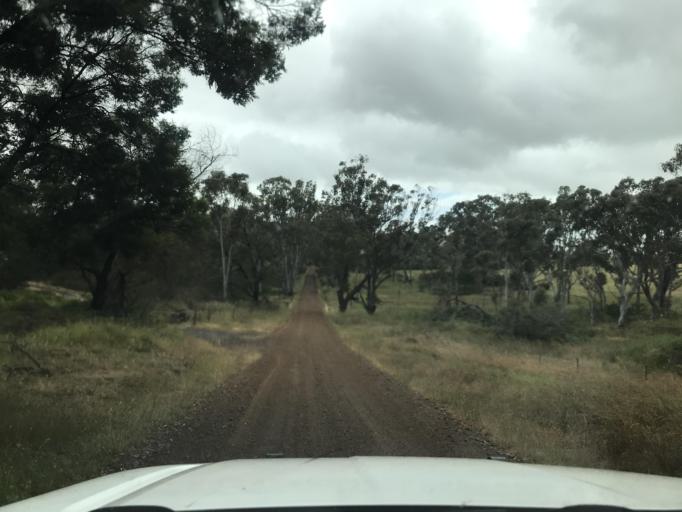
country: AU
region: South Australia
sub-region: Wattle Range
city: Penola
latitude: -37.2345
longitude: 141.4345
